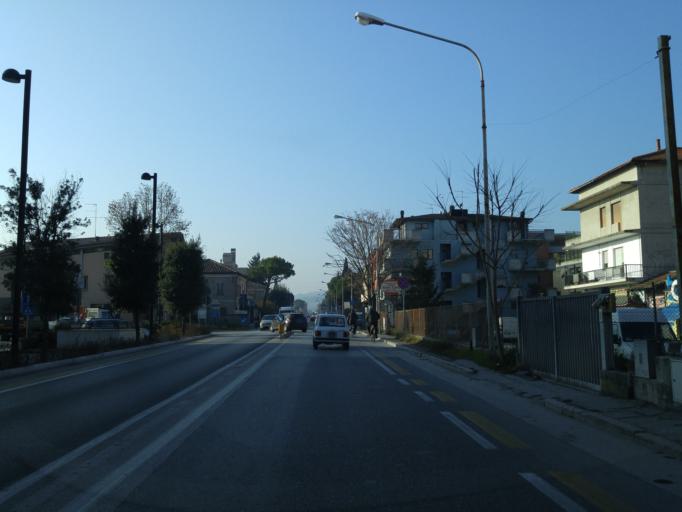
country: IT
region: The Marches
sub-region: Provincia di Pesaro e Urbino
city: Fano
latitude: 43.8393
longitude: 13.0099
